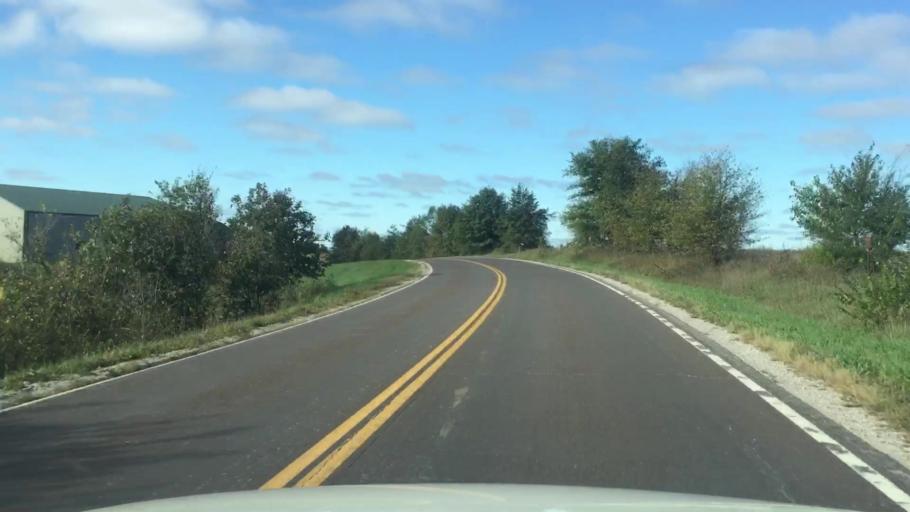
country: US
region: Missouri
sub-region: Howard County
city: Fayette
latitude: 39.0986
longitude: -92.7389
